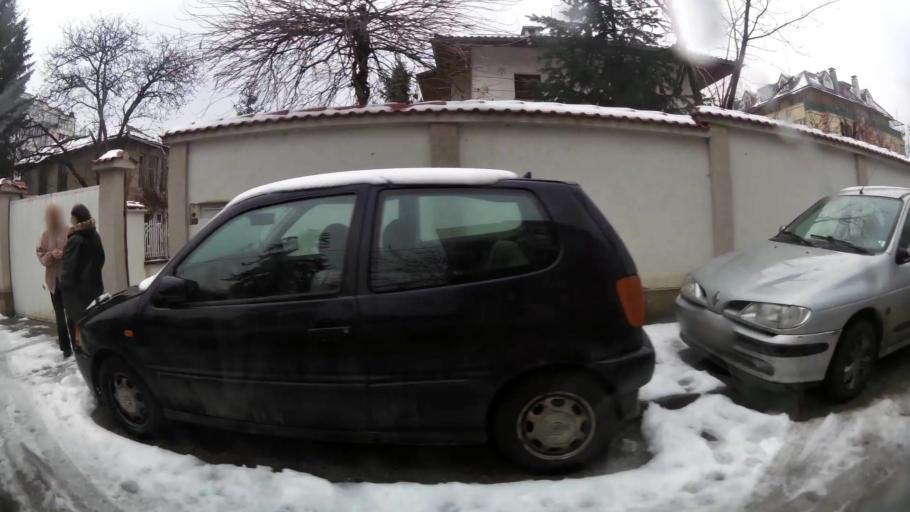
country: BG
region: Sofia-Capital
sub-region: Stolichna Obshtina
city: Sofia
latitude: 42.6617
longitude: 23.2700
